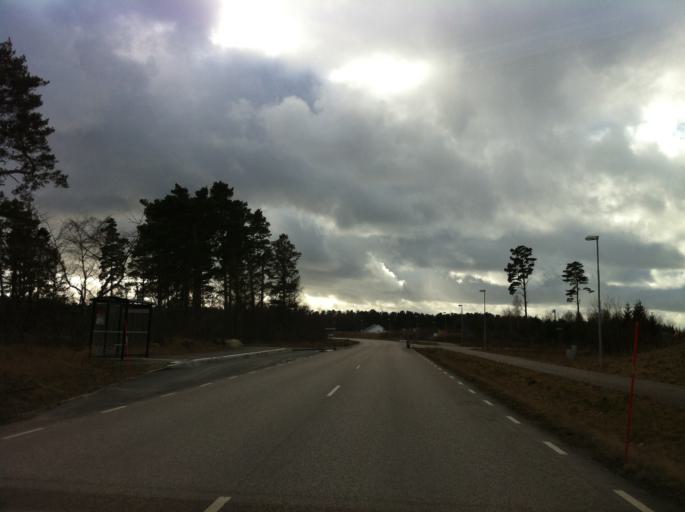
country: SE
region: Skane
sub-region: Bromolla Kommun
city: Bromoella
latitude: 56.0564
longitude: 14.4487
